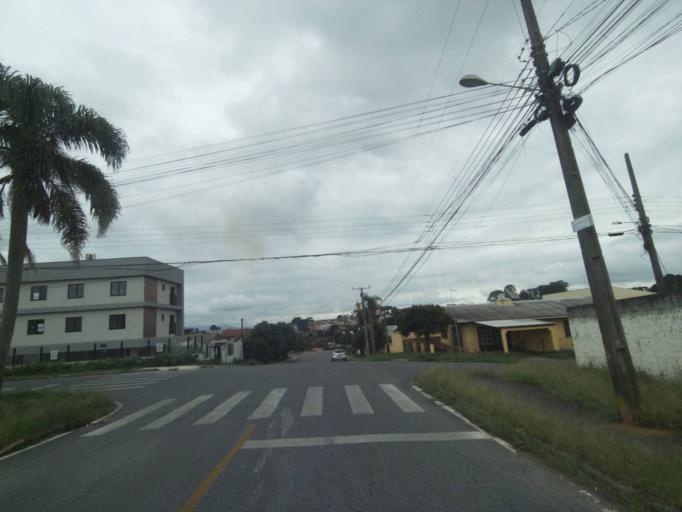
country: BR
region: Parana
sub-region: Quatro Barras
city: Quatro Barras
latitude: -25.3523
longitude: -49.1179
